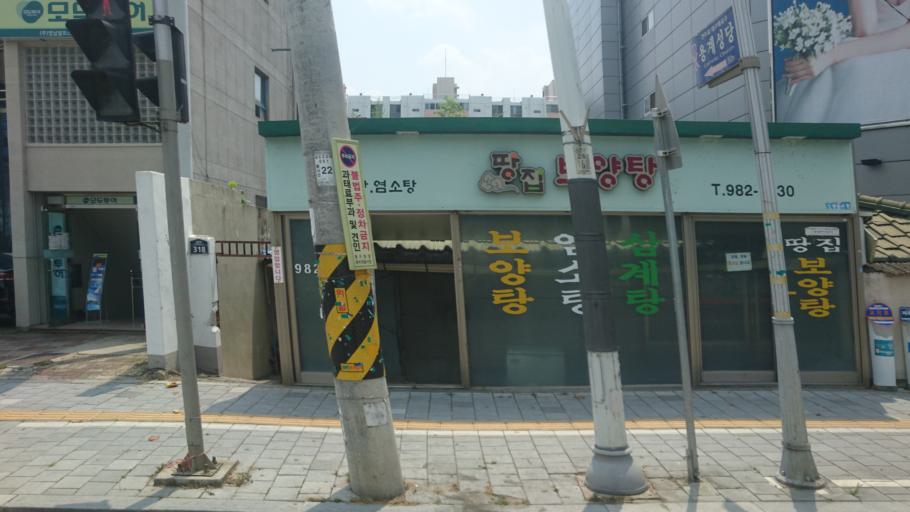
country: KR
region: Daegu
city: Daegu
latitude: 35.8783
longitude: 128.6743
